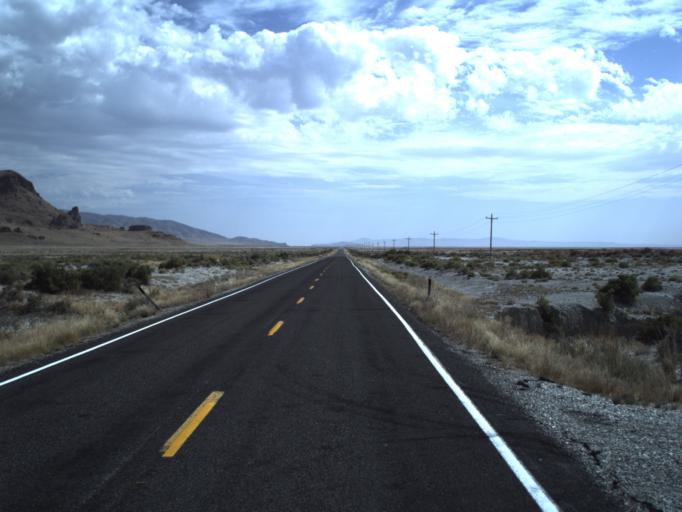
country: US
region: Utah
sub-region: Tooele County
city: Wendover
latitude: 41.4244
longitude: -113.8619
